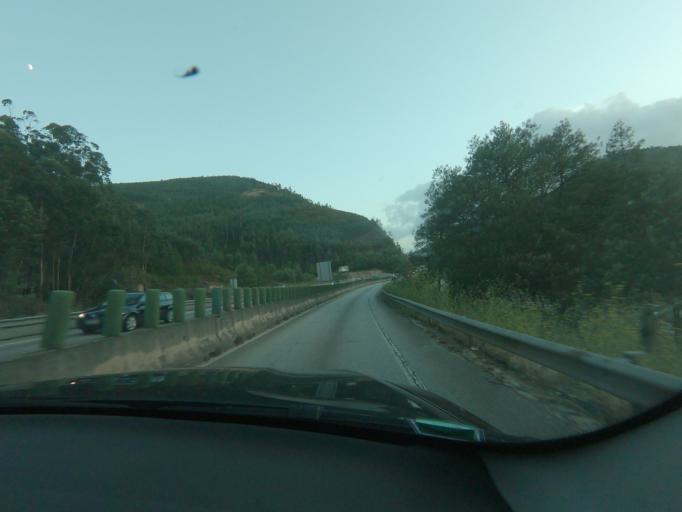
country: PT
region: Coimbra
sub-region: Penacova
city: Penacova
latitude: 40.2892
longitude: -8.2580
